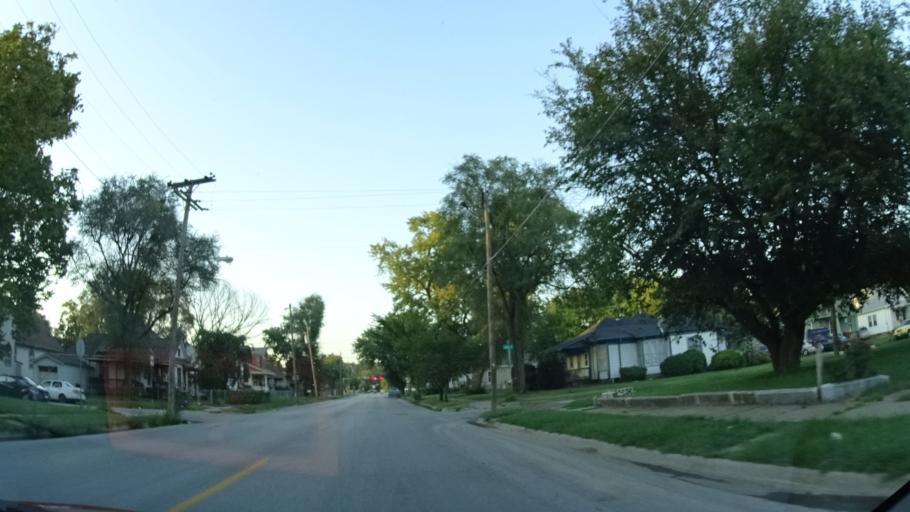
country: US
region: Iowa
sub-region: Pottawattamie County
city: Council Bluffs
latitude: 41.2658
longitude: -95.8560
